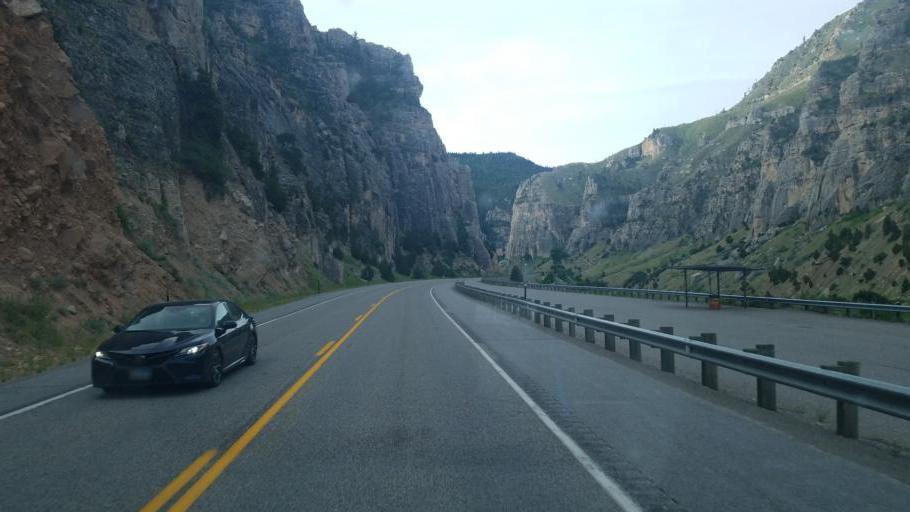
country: US
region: Wyoming
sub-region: Hot Springs County
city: Thermopolis
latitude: 43.5372
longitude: -108.1797
